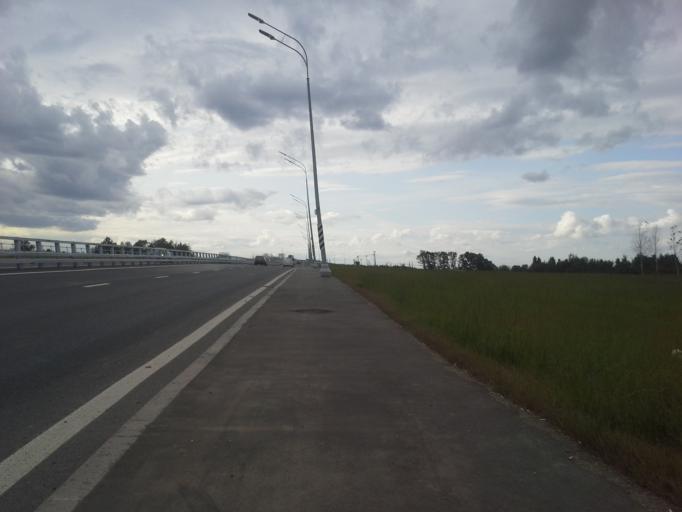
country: RU
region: Moskovskaya
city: Kokoshkino
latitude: 55.5886
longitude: 37.1576
